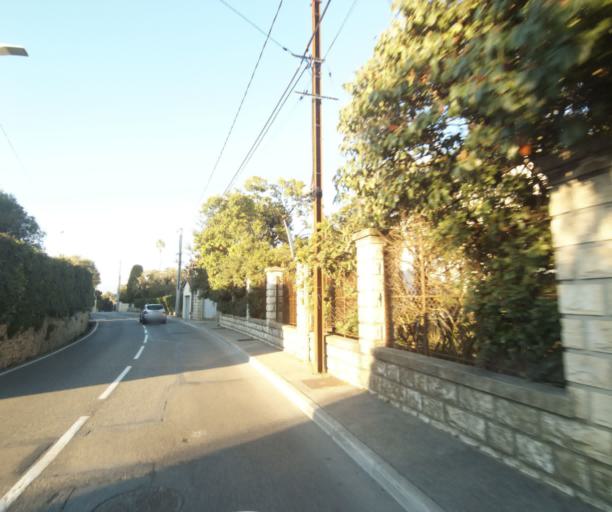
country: FR
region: Provence-Alpes-Cote d'Azur
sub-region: Departement des Alpes-Maritimes
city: Antibes
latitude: 43.5667
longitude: 7.1249
